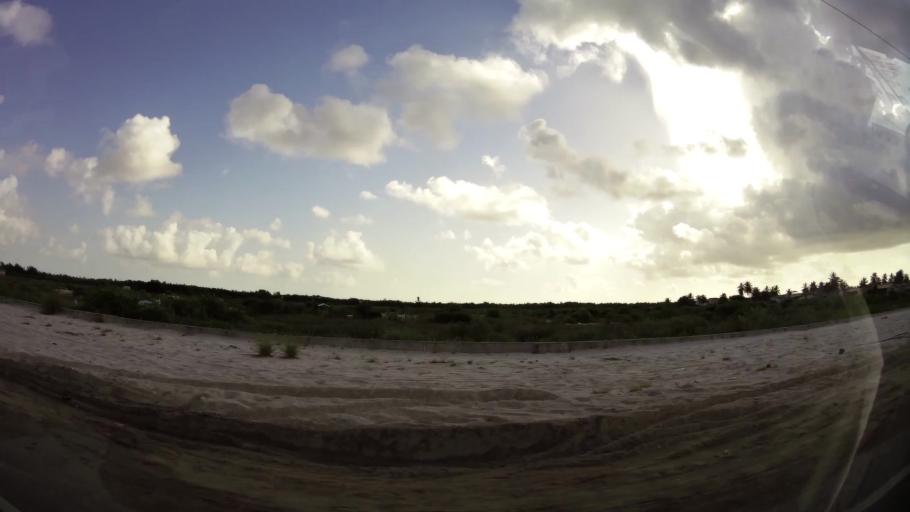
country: GY
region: Demerara-Mahaica
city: Georgetown
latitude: 6.8013
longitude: -58.0433
